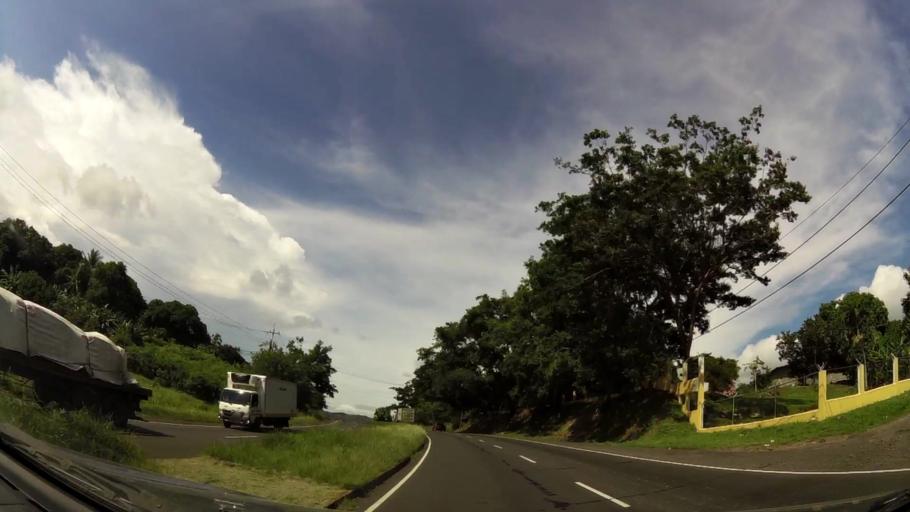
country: PA
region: Panama
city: Capira
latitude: 8.6766
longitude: -79.8686
